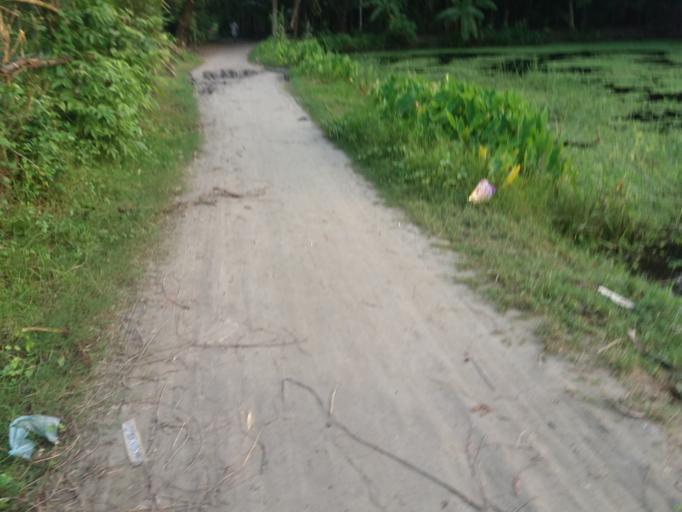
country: BD
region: Chittagong
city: Feni
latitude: 22.9372
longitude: 91.3527
